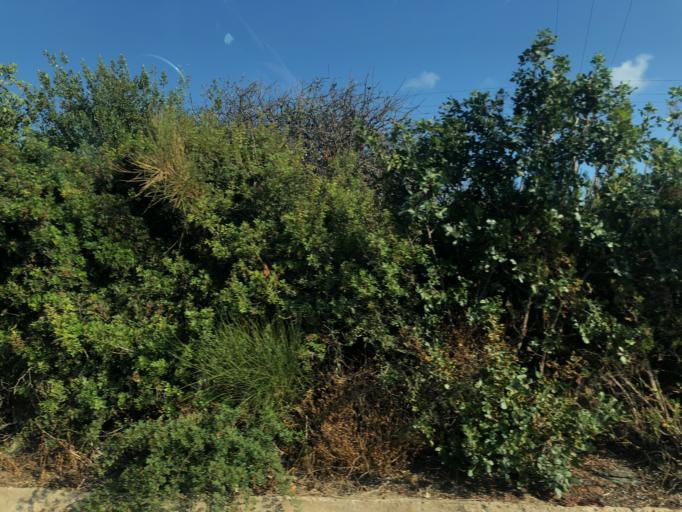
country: GR
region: Crete
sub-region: Nomos Rethymnis
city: Atsipopoulon
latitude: 35.3653
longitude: 24.4241
